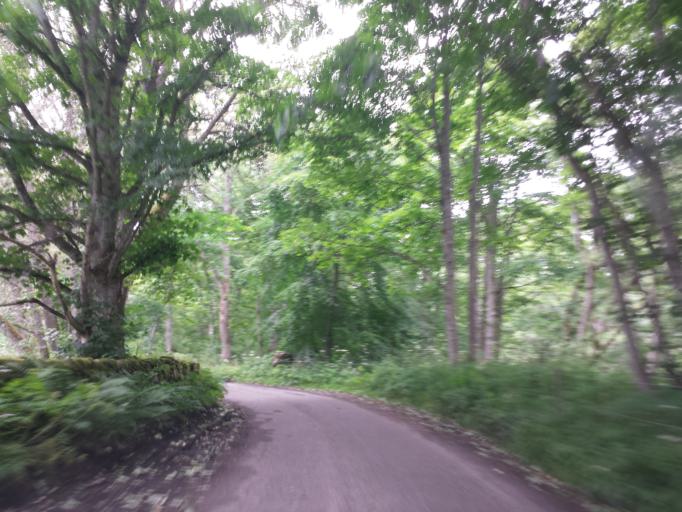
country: GB
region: Scotland
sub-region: Highland
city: Nairn
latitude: 57.5074
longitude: -4.0016
